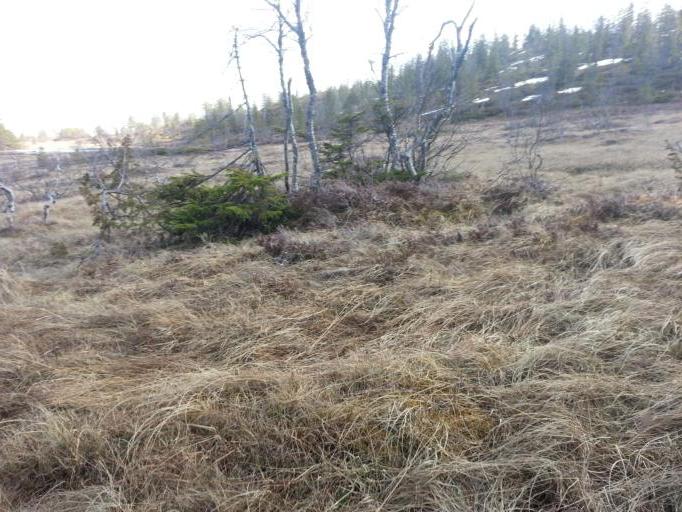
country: NO
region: Nord-Trondelag
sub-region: Levanger
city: Skogn
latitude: 63.5908
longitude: 11.0791
